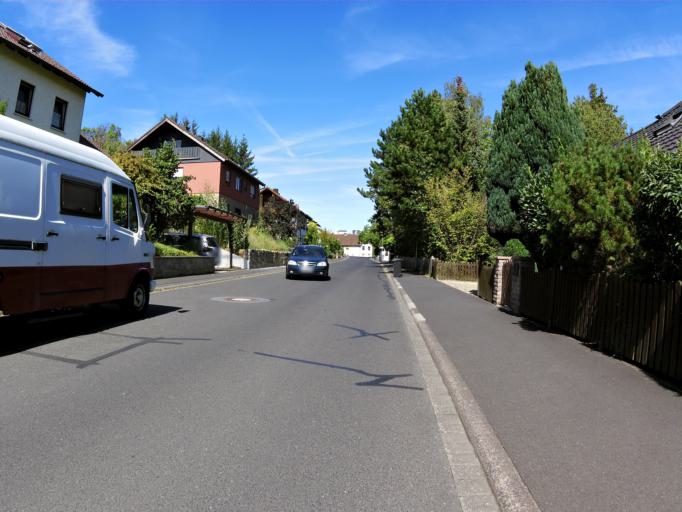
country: DE
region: Bavaria
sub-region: Regierungsbezirk Unterfranken
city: Guntersleben
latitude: 49.8670
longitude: 9.9014
